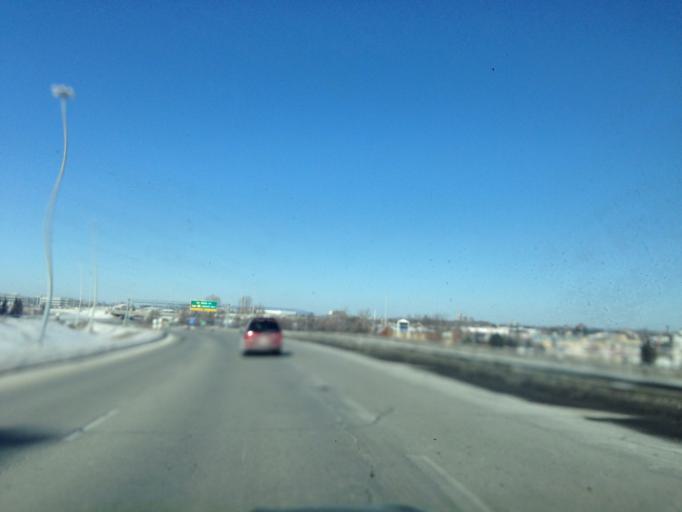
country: CA
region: Ontario
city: Ottawa
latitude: 45.4123
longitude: -75.6022
